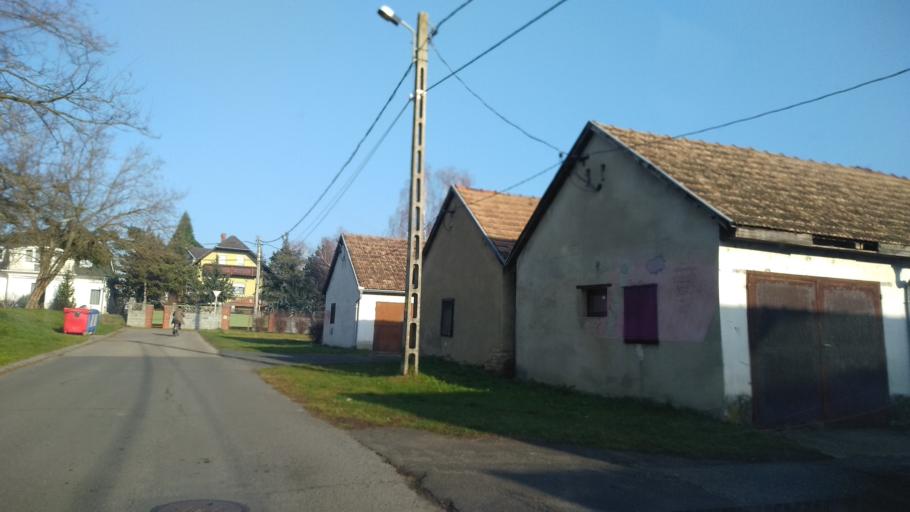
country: HU
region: Somogy
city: Barcs
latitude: 45.9607
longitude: 17.4678
